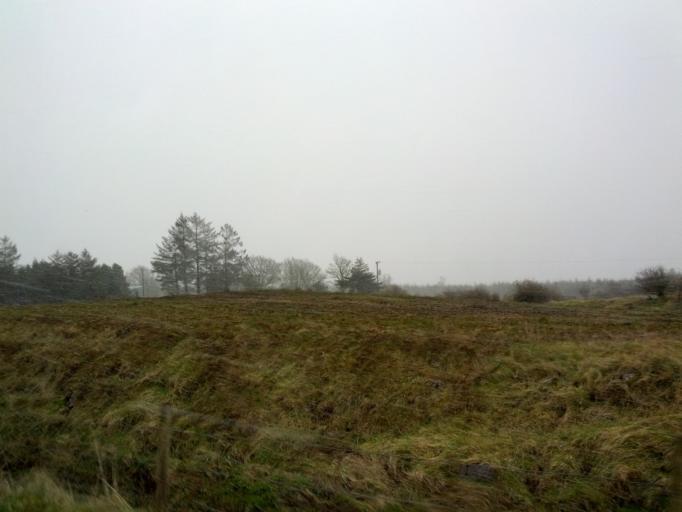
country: IE
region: Connaught
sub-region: County Galway
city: Athenry
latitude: 53.4022
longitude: -8.6047
